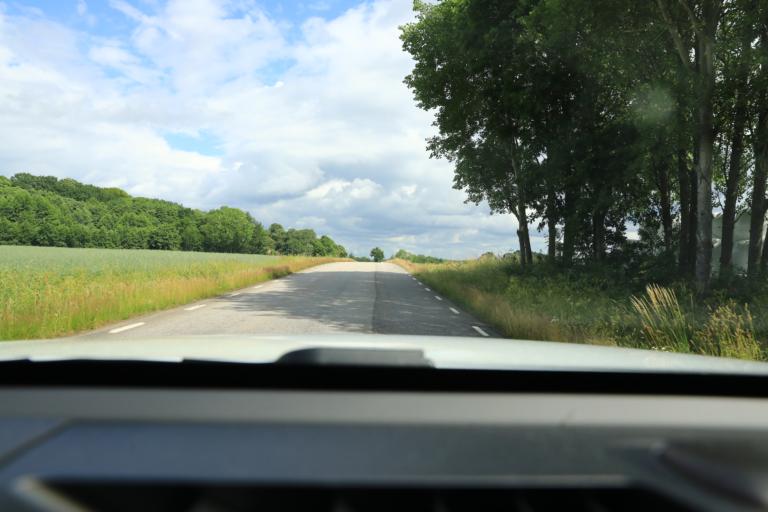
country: SE
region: Halland
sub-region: Varbergs Kommun
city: Tvaaker
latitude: 57.0854
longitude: 12.4034
